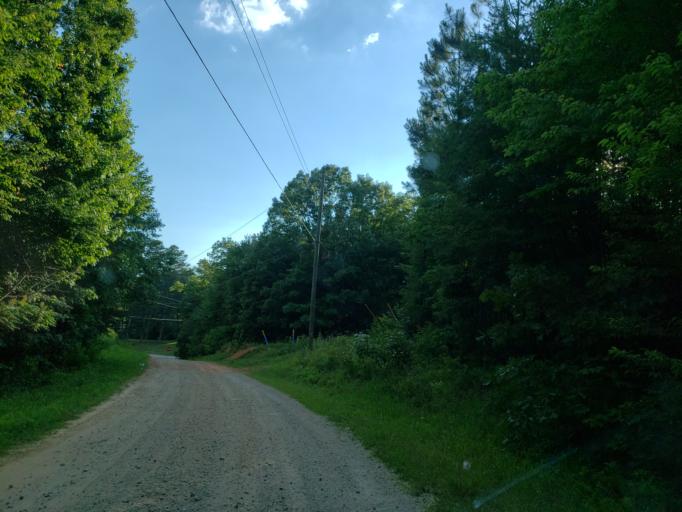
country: US
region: Georgia
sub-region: Haralson County
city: Buchanan
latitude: 33.9024
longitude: -85.3115
